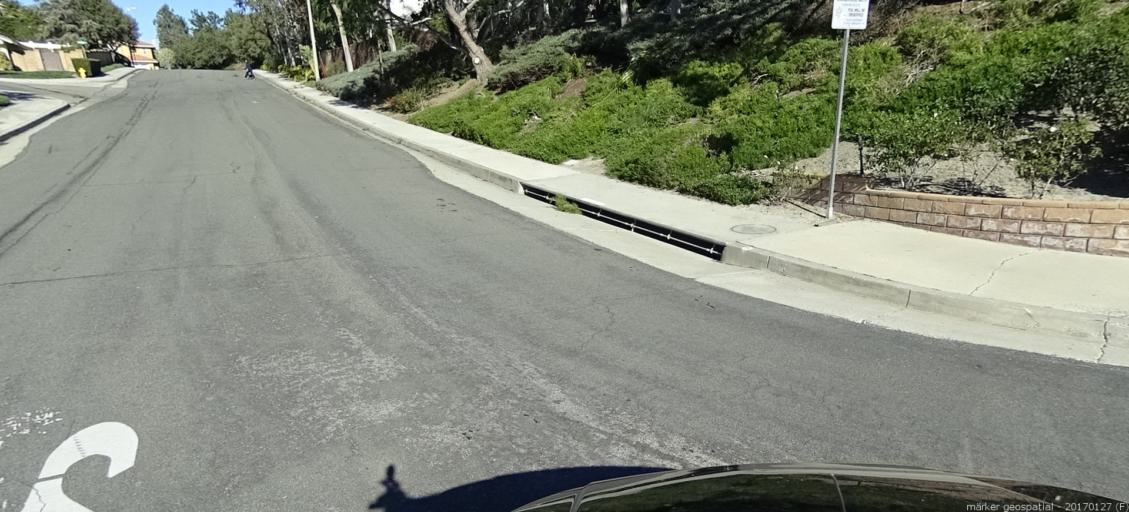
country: US
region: California
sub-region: Orange County
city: Foothill Ranch
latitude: 33.6574
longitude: -117.6613
